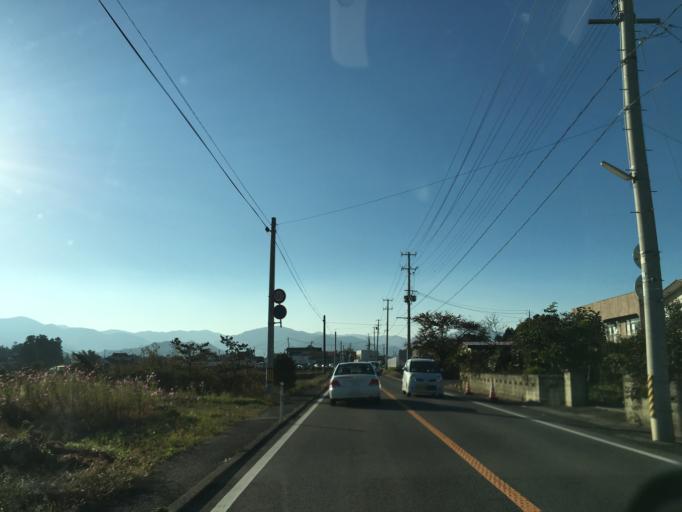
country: JP
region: Fukushima
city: Koriyama
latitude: 37.3923
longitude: 140.2915
